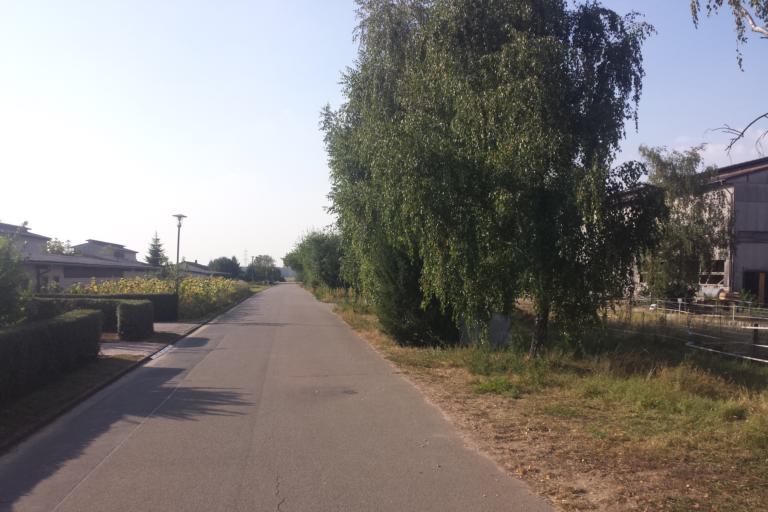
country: DE
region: Baden-Wuerttemberg
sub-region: Karlsruhe Region
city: Plankstadt
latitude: 49.4068
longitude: 8.5861
